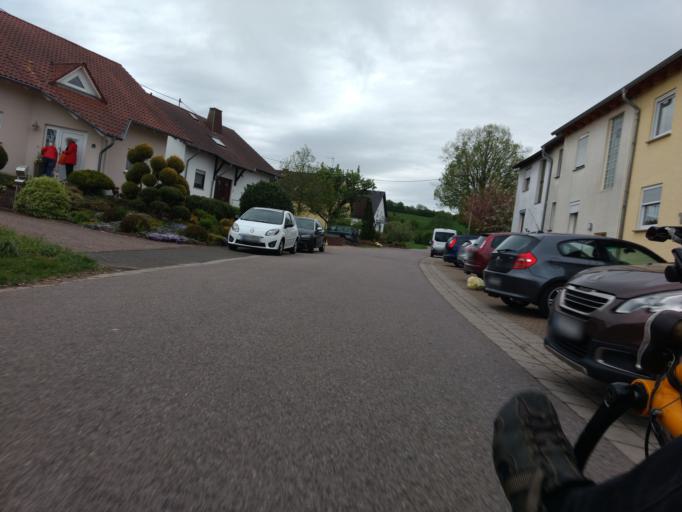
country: DE
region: Saarland
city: Rehlingen-Siersburg
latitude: 49.3277
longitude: 6.6553
